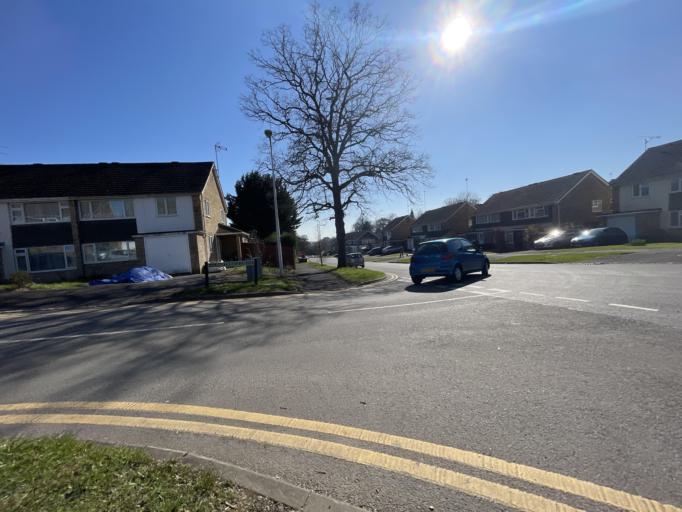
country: GB
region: England
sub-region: West Berkshire
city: Tilehurst
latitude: 51.4513
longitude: -1.0526
